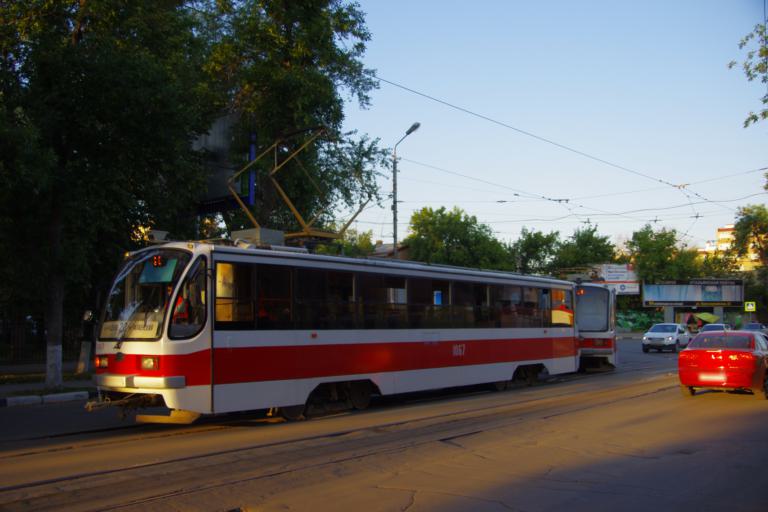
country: RU
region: Samara
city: Samara
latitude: 53.1930
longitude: 50.1022
